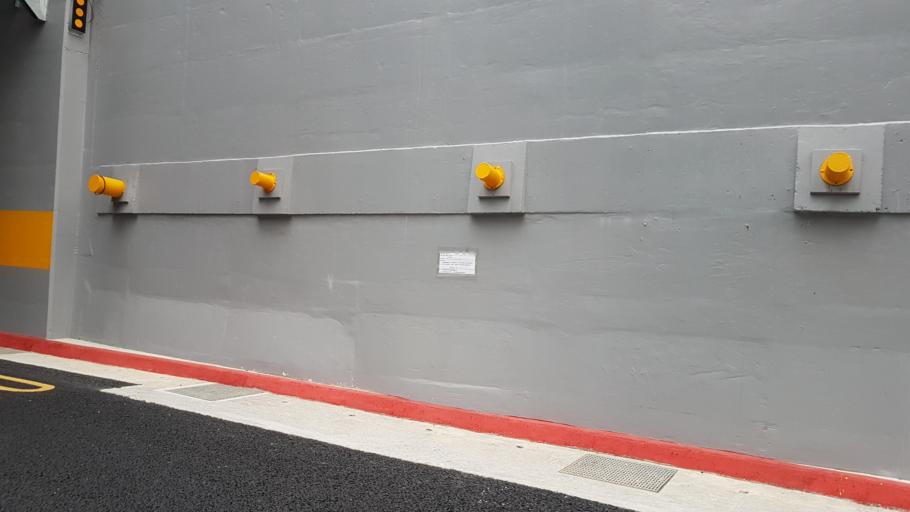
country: TW
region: Taipei
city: Taipei
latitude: 25.0032
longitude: 121.5479
